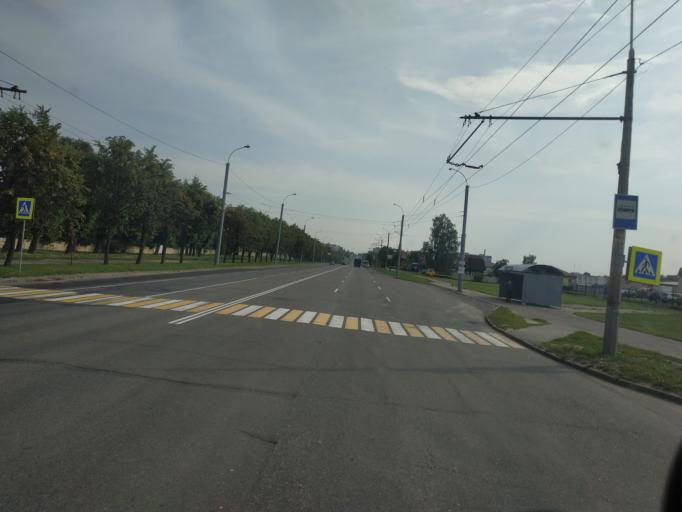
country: BY
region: Mogilev
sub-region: Mahilyowski Rayon
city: Veyno
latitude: 53.8667
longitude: 30.3623
